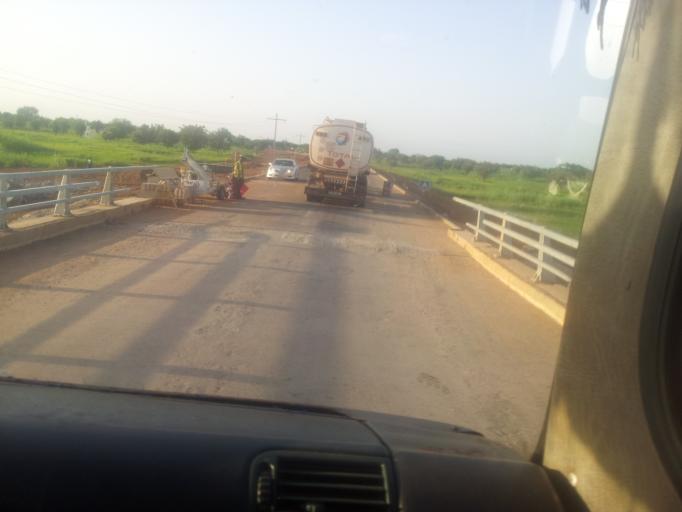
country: BF
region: Centre-Est
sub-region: Kouritenga Province
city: Koupela
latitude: 12.0127
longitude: -0.3615
